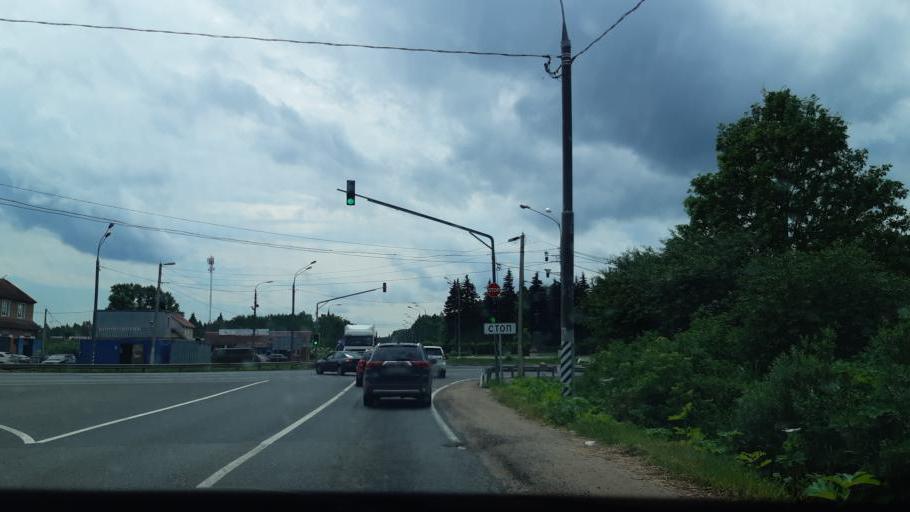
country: RU
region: Moskovskaya
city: Dorokhovo
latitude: 55.5317
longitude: 36.3597
